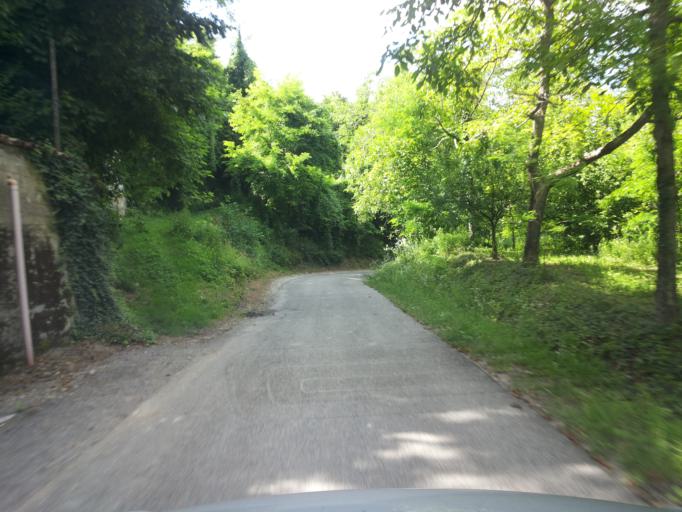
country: IT
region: Piedmont
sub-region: Provincia di Alessandria
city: Serralunga di Crea
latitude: 45.1028
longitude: 8.2752
